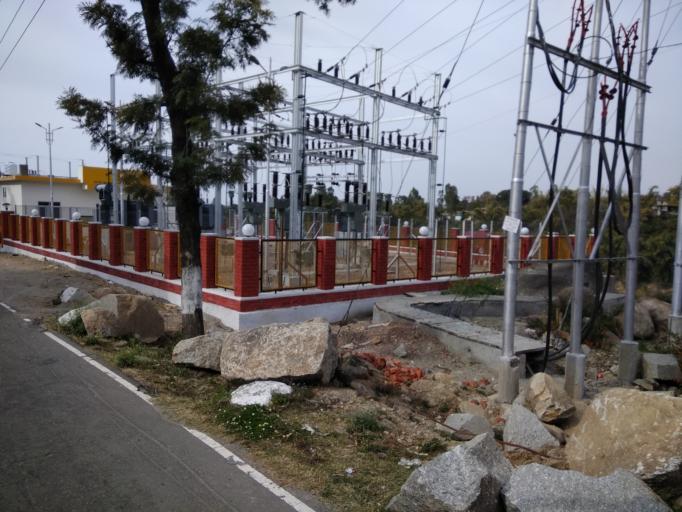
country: IN
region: Himachal Pradesh
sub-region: Kangra
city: Dharmsala
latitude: 32.1599
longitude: 76.4067
